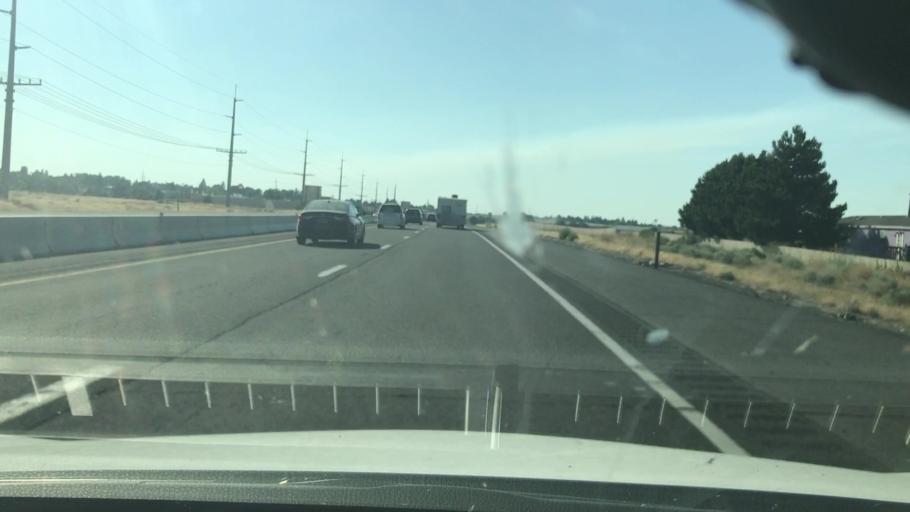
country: US
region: Washington
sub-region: Grant County
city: Moses Lake
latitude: 47.1466
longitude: -119.2863
